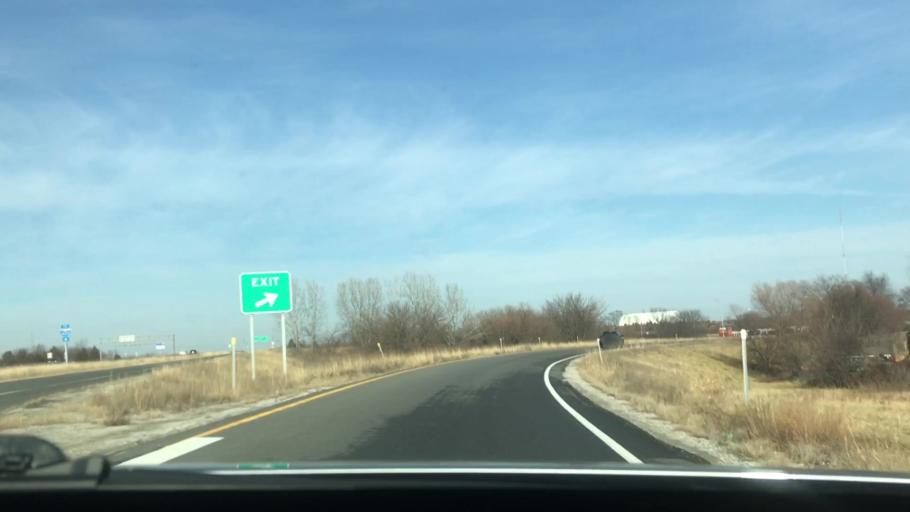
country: US
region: Missouri
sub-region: Clay County
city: Smithville
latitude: 39.3003
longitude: -94.5844
